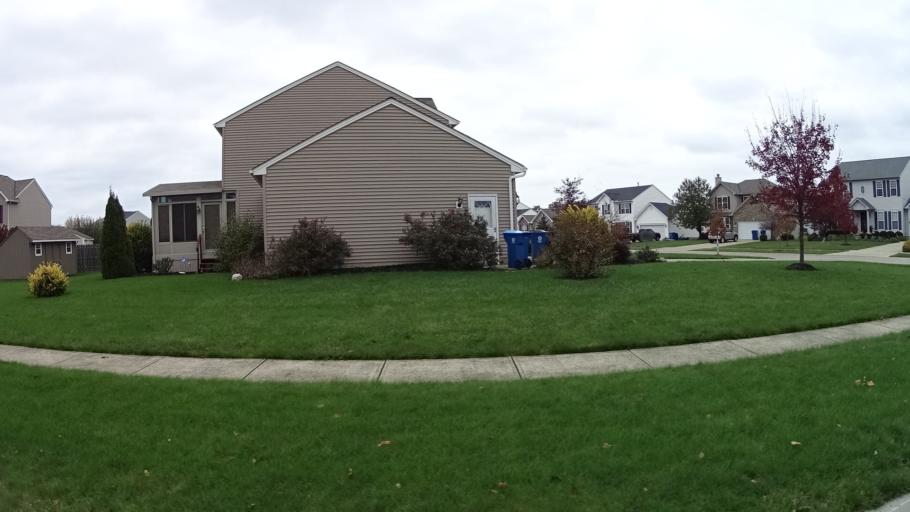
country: US
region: Ohio
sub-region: Lorain County
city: Lorain
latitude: 41.4396
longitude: -82.2205
